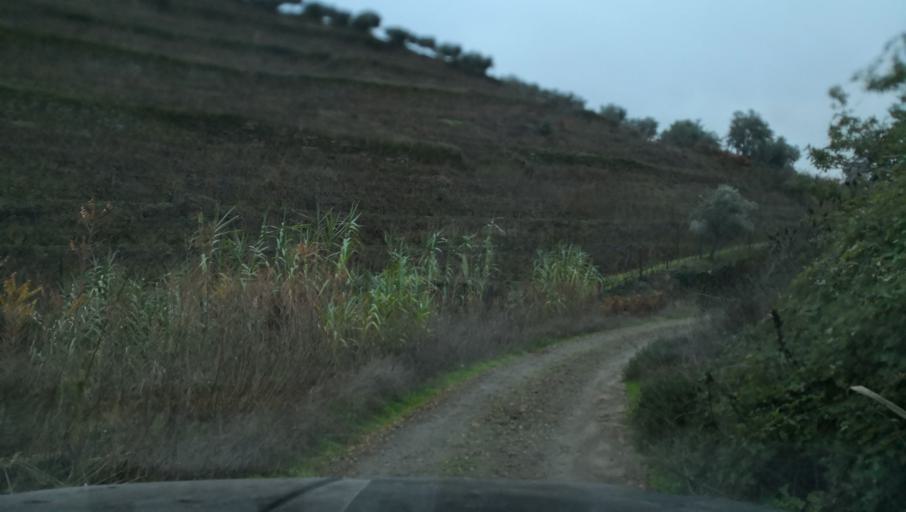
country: PT
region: Vila Real
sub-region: Santa Marta de Penaguiao
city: Santa Marta de Penaguiao
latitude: 41.2057
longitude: -7.7597
